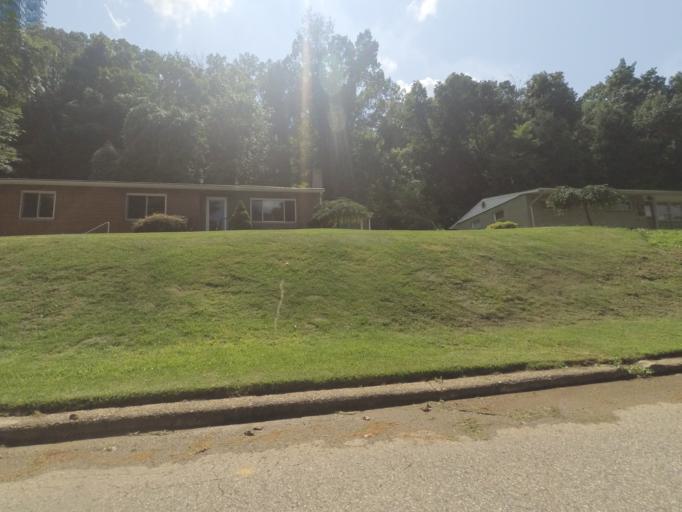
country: US
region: West Virginia
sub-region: Cabell County
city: Huntington
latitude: 38.3959
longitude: -82.4273
